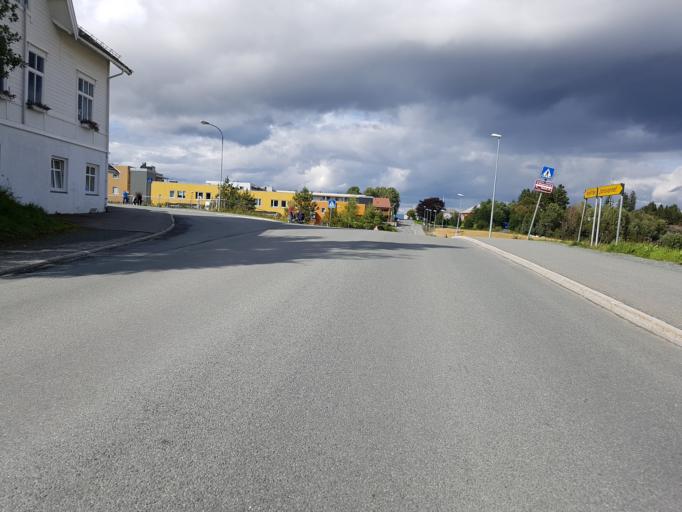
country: NO
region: Sor-Trondelag
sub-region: Trondheim
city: Trondheim
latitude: 63.4127
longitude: 10.4750
